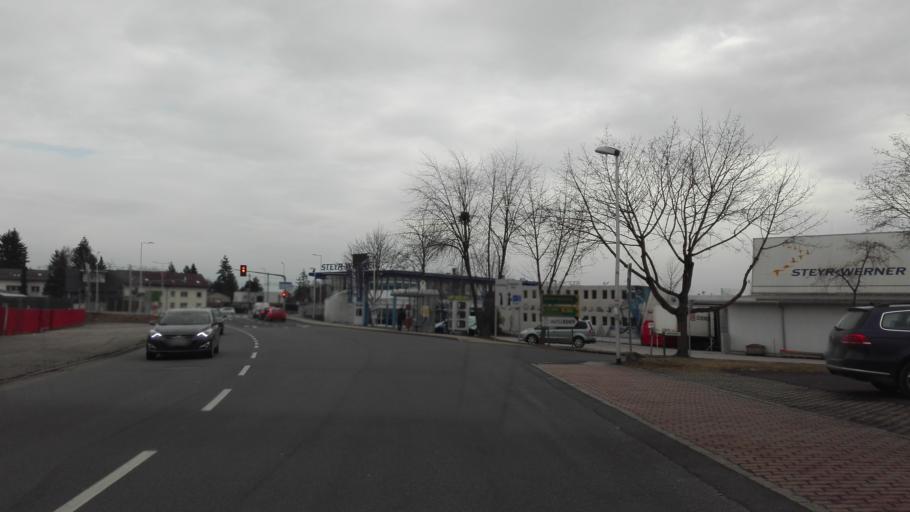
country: AT
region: Upper Austria
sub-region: Politischer Bezirk Linz-Land
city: Traun
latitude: 48.2382
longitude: 14.2328
